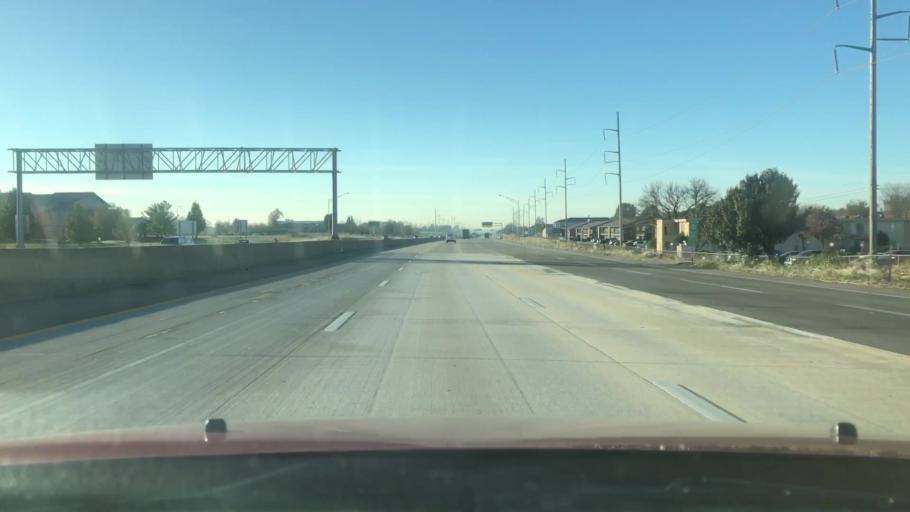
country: US
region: Missouri
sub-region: Greene County
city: Springfield
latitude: 37.1770
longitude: -93.2244
